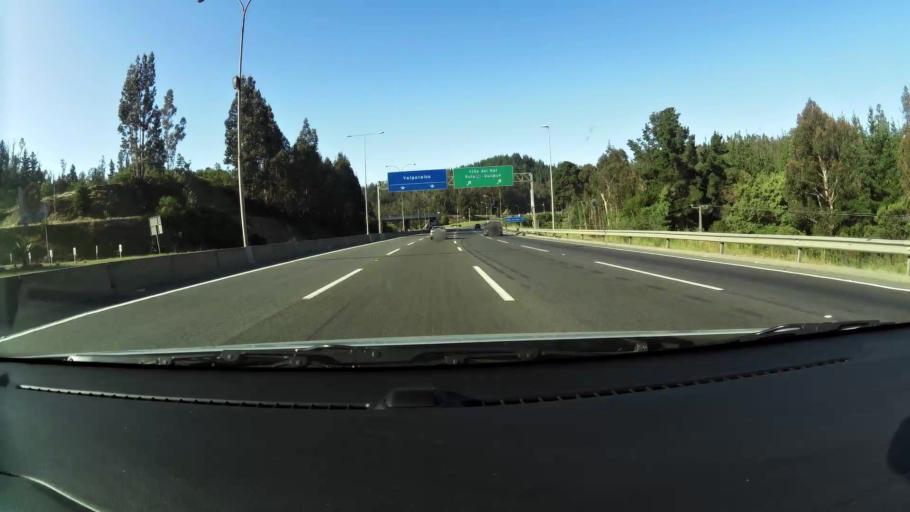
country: CL
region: Valparaiso
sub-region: Provincia de Valparaiso
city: Vina del Mar
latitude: -33.0993
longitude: -71.5477
